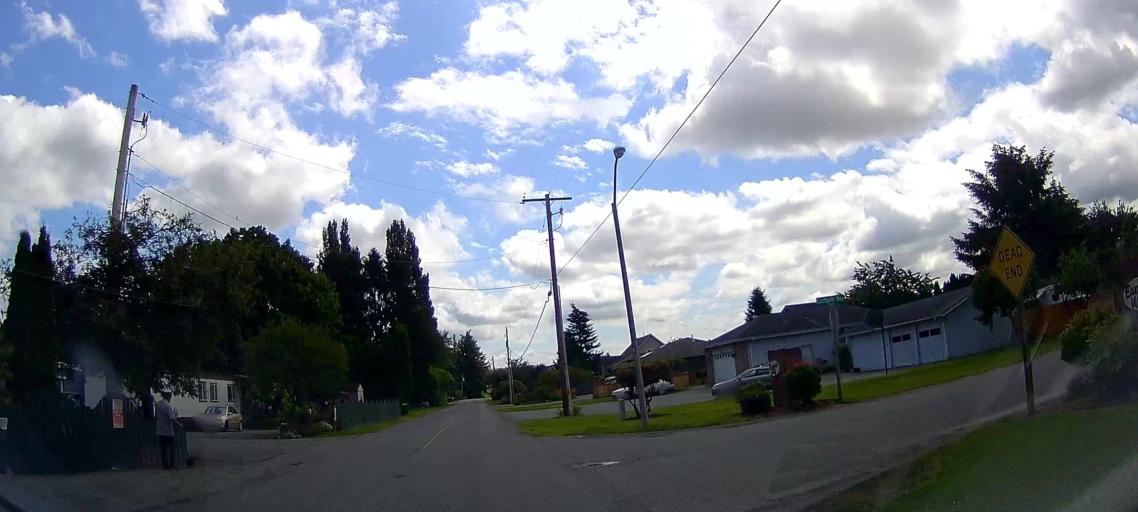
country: US
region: Washington
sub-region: Skagit County
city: Burlington
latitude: 48.4812
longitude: -122.3030
